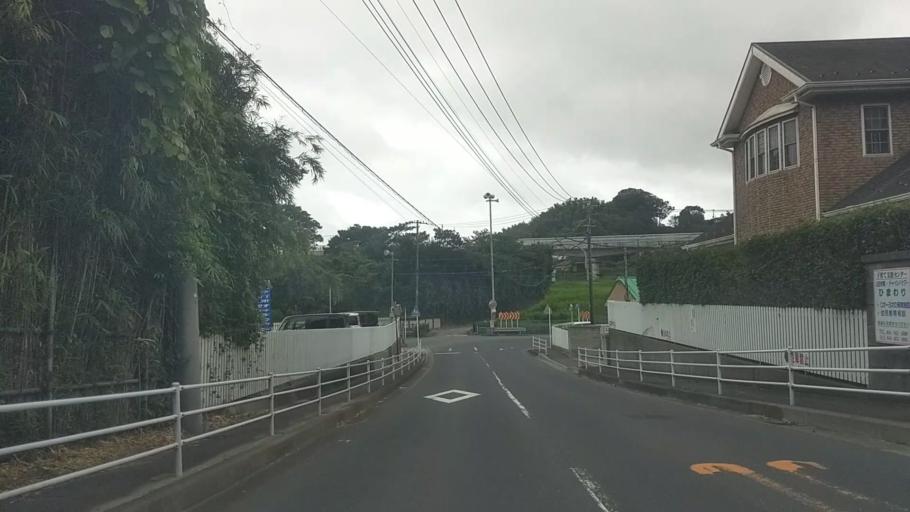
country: JP
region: Kanagawa
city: Yokosuka
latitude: 35.2330
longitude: 139.6449
